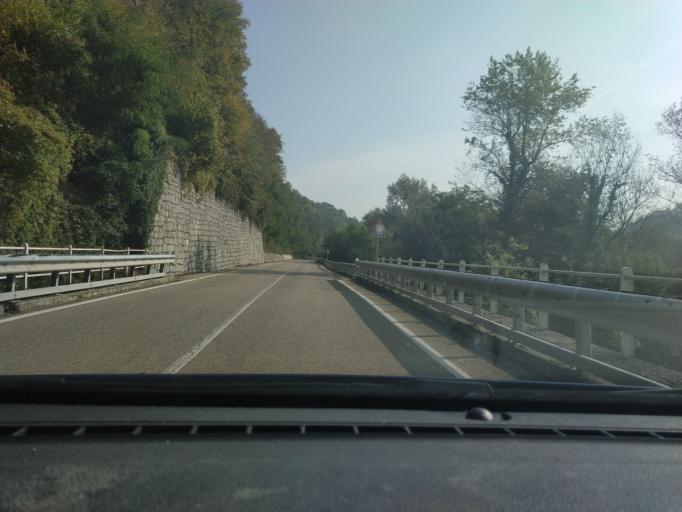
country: IT
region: Piedmont
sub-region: Provincia di Biella
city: Sala Biellese
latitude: 45.5181
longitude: 7.9730
